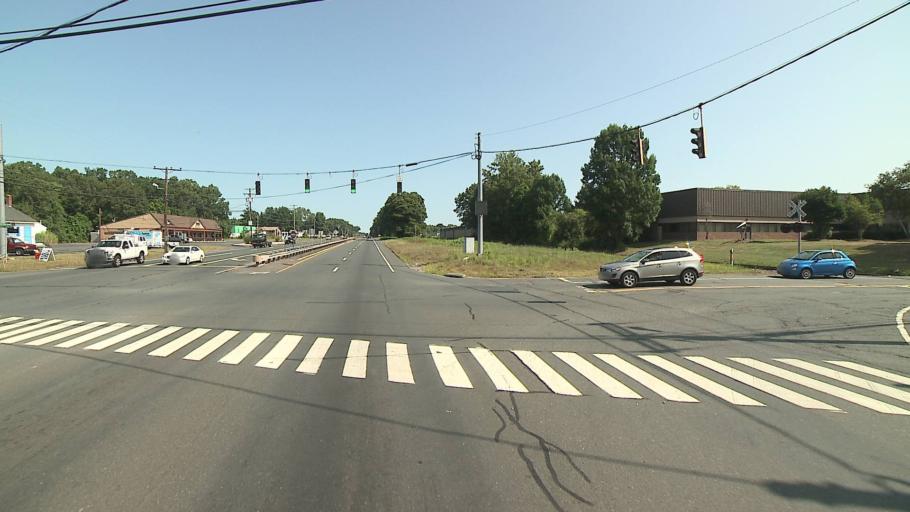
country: US
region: Connecticut
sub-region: Hartford County
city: South Windsor
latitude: 41.8192
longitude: -72.6093
